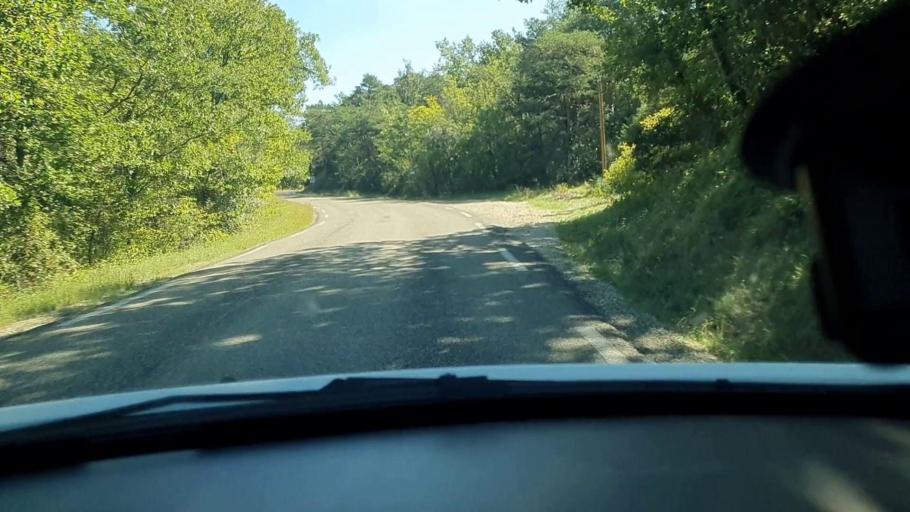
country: FR
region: Languedoc-Roussillon
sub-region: Departement du Gard
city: Goudargues
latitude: 44.1750
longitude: 4.4836
